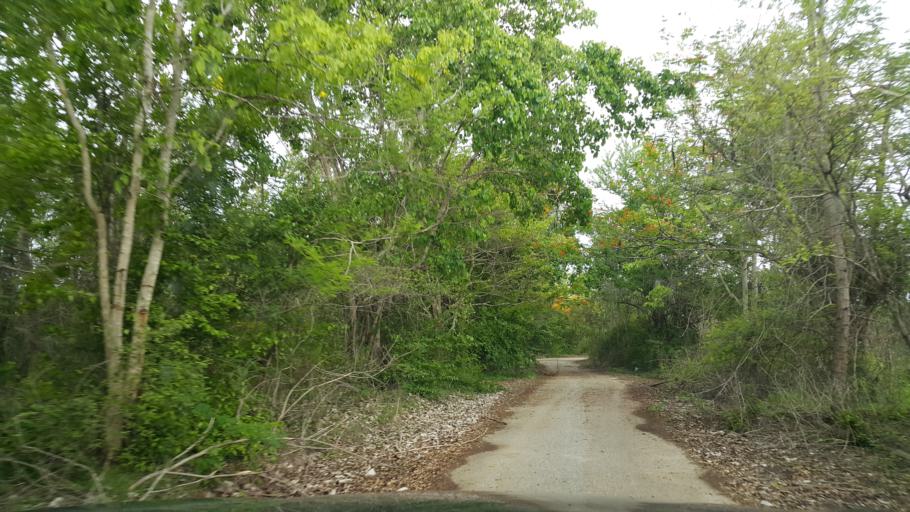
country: TH
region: Chiang Mai
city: San Kamphaeng
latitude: 18.7588
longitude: 99.1179
